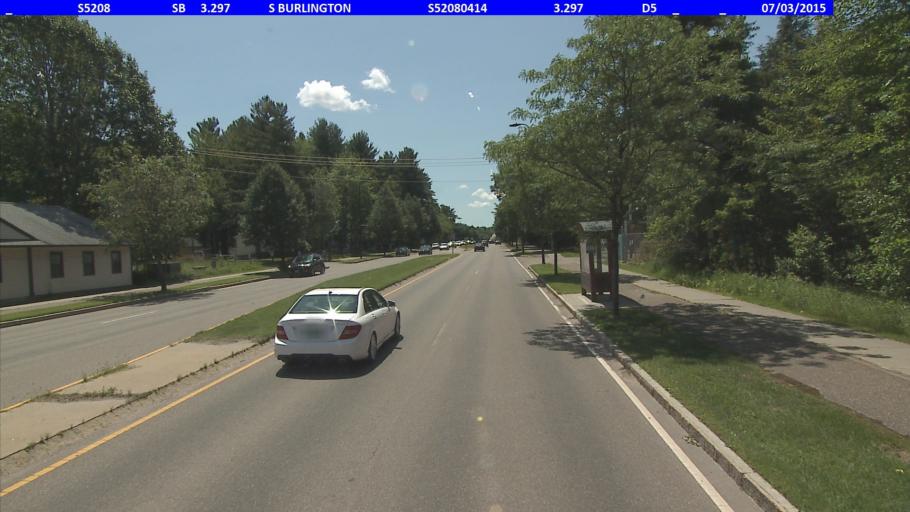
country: US
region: Vermont
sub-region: Chittenden County
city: South Burlington
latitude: 44.4577
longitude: -73.1796
